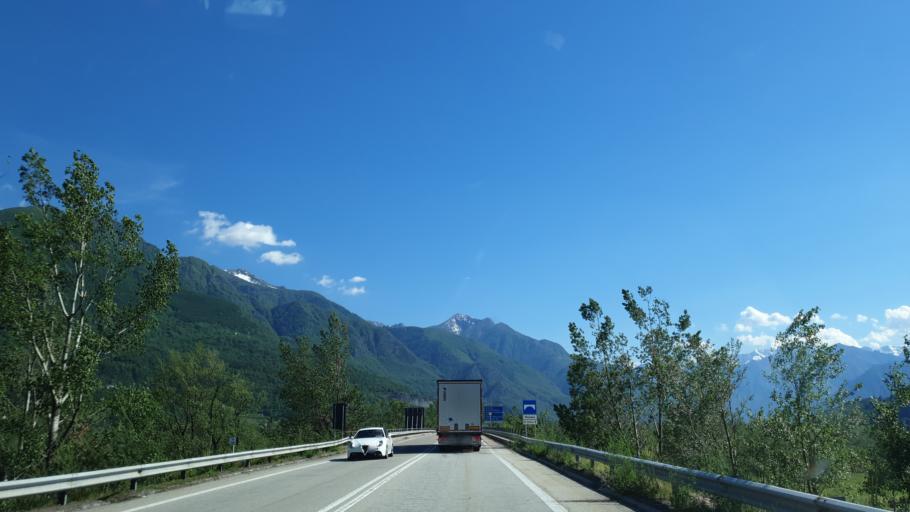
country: IT
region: Piedmont
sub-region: Provincia Verbano-Cusio-Ossola
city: Masera
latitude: 46.1337
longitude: 8.3079
